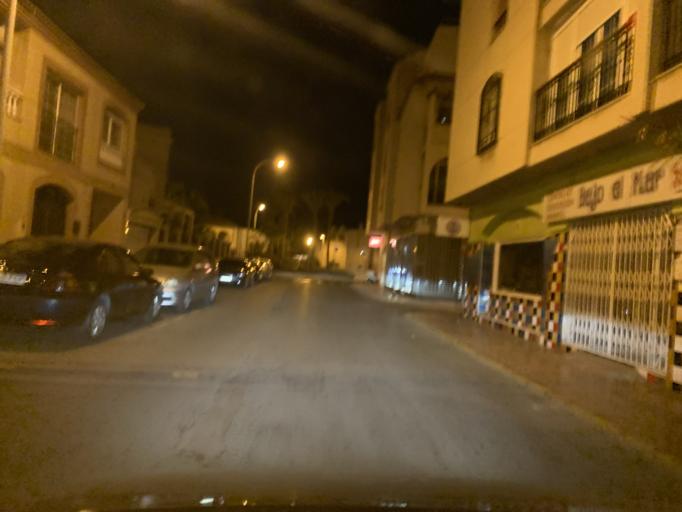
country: ES
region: Andalusia
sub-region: Provincia de Almeria
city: Roquetas de Mar
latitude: 36.7660
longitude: -2.6097
